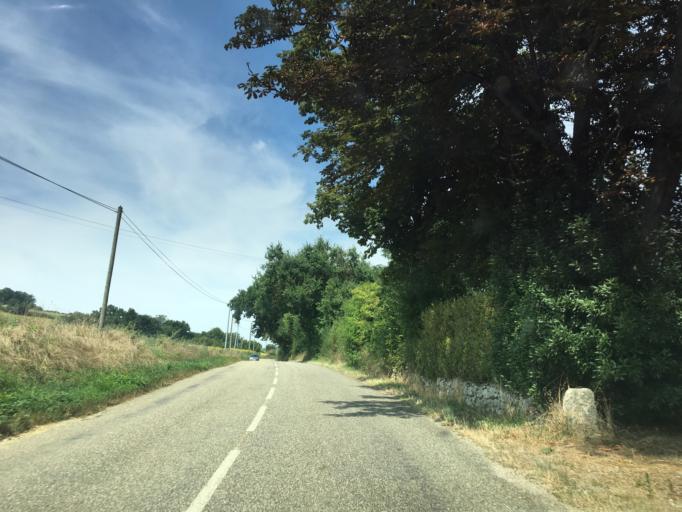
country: FR
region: Midi-Pyrenees
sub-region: Departement du Gers
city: Fleurance
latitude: 43.9004
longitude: 0.7722
